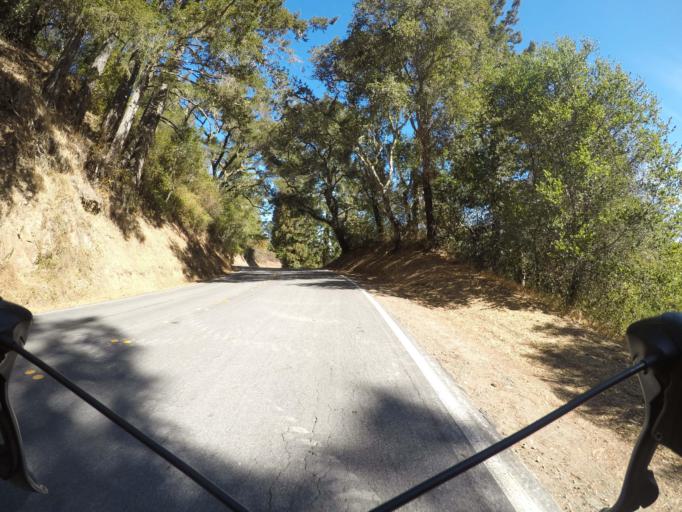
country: US
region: California
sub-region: San Mateo County
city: Portola Valley
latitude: 37.2991
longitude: -122.2764
